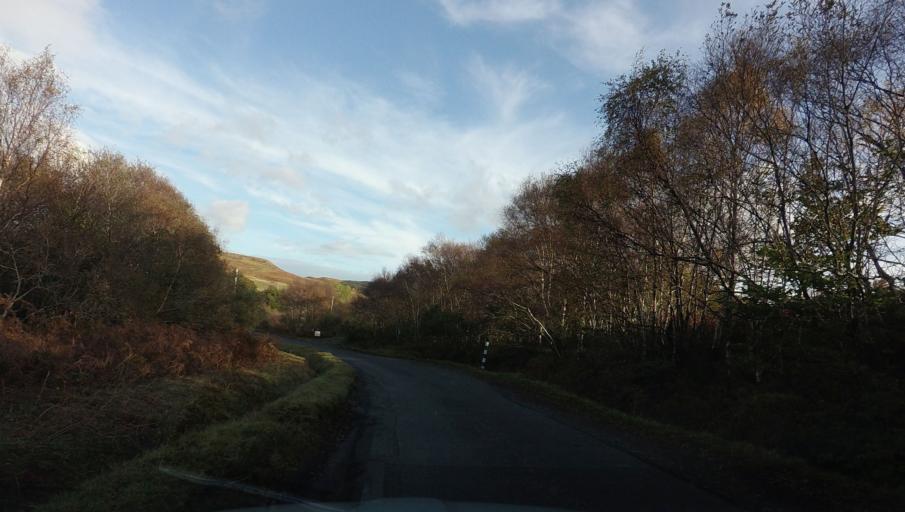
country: GB
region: Scotland
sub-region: Argyll and Bute
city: Isle Of Mull
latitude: 56.3420
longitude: -6.1046
